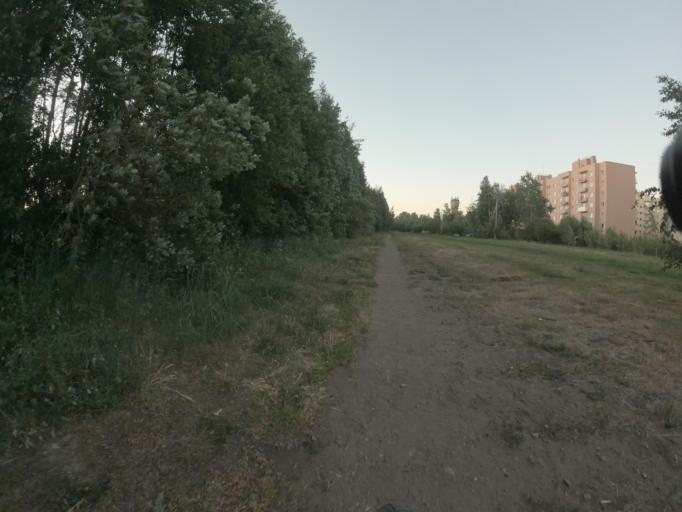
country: RU
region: St.-Petersburg
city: Krasnogvargeisky
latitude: 59.9844
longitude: 30.5247
